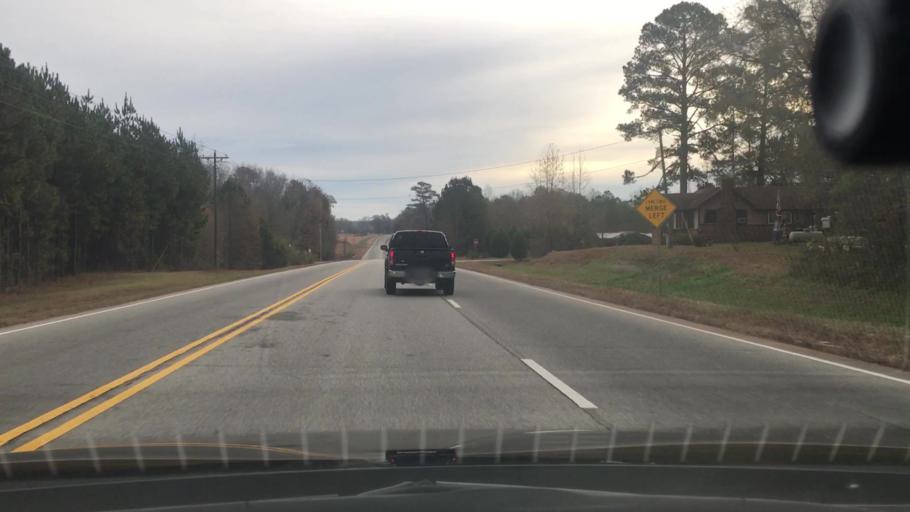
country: US
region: Georgia
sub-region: Coweta County
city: Senoia
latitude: 33.2487
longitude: -84.4527
